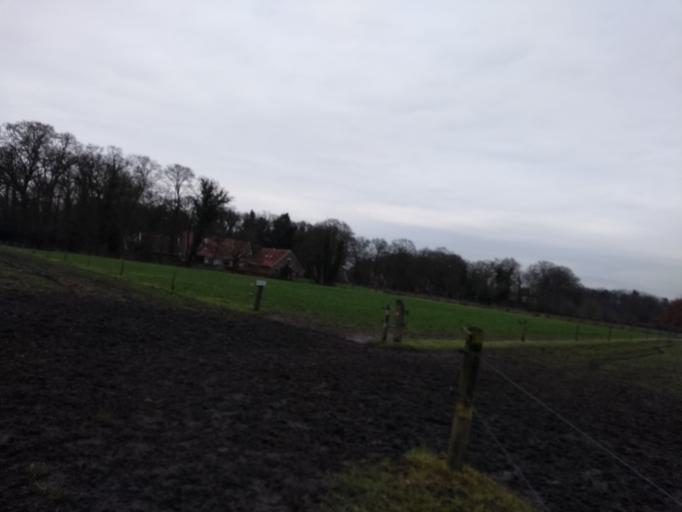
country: NL
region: Overijssel
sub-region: Gemeente Hengelo
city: Hengelo
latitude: 52.2282
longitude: 6.8075
